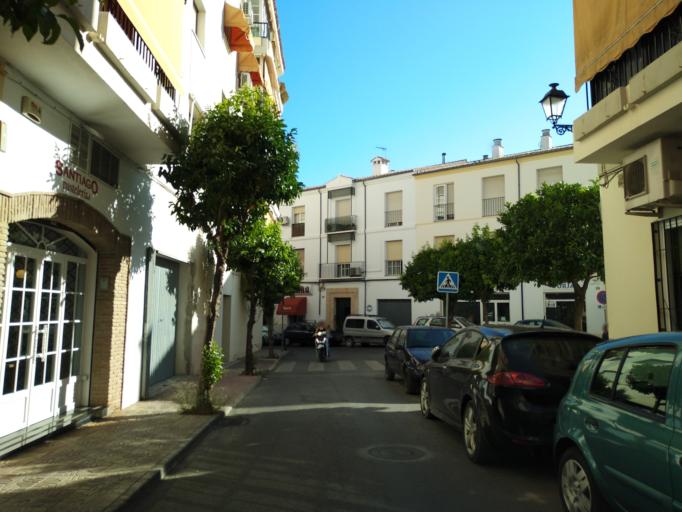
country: ES
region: Andalusia
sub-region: Provincia de Malaga
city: Antequera
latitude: 37.0185
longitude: -4.5650
